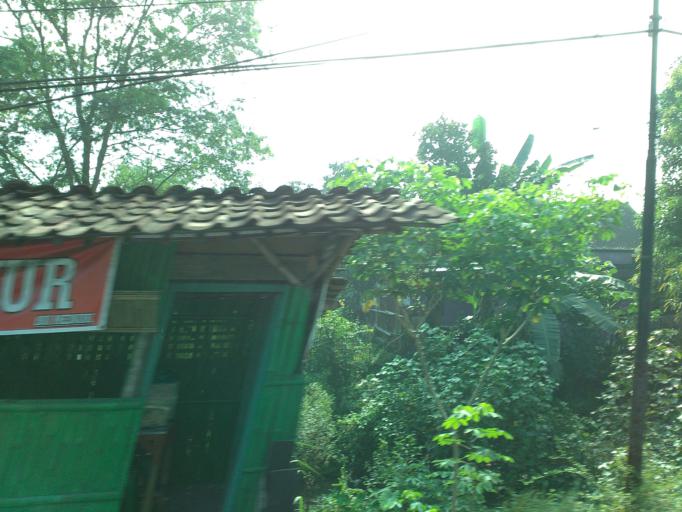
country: ID
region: Central Java
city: Gatak
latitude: -7.6032
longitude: 110.7028
